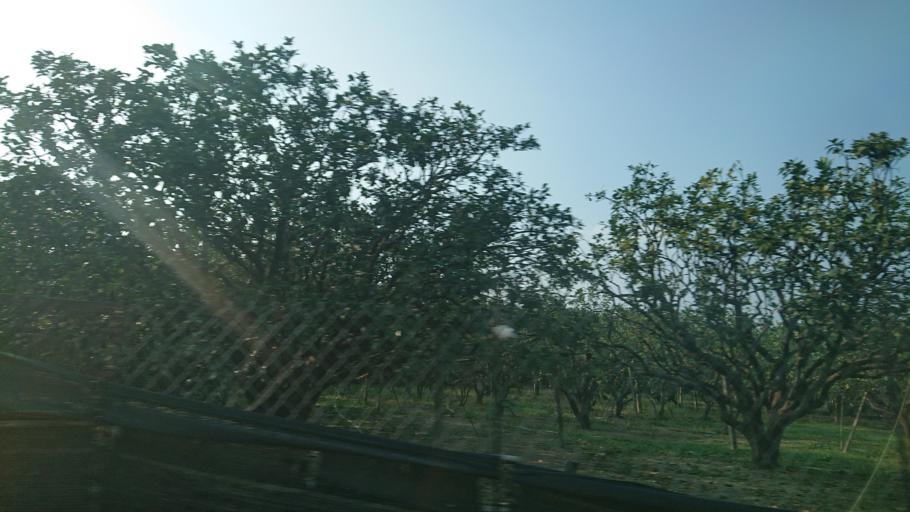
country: TW
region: Taiwan
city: Xinying
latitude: 23.1631
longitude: 120.2510
